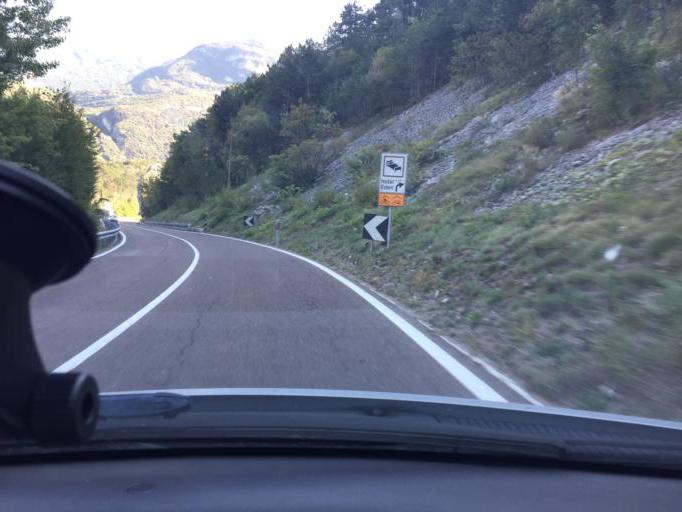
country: IT
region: Trentino-Alto Adige
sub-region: Provincia di Trento
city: Dro
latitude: 45.9784
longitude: 10.9234
